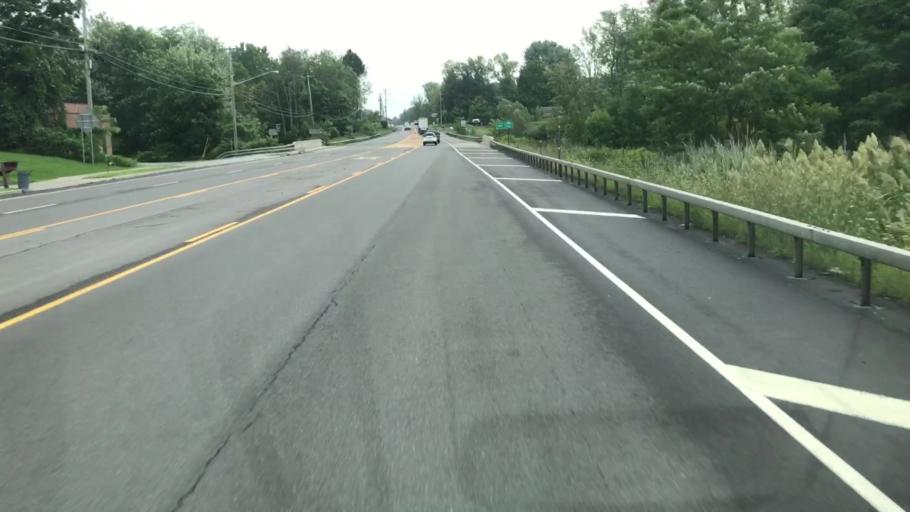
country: US
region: New York
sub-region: Onondaga County
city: Liverpool
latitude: 43.1862
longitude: -76.2152
